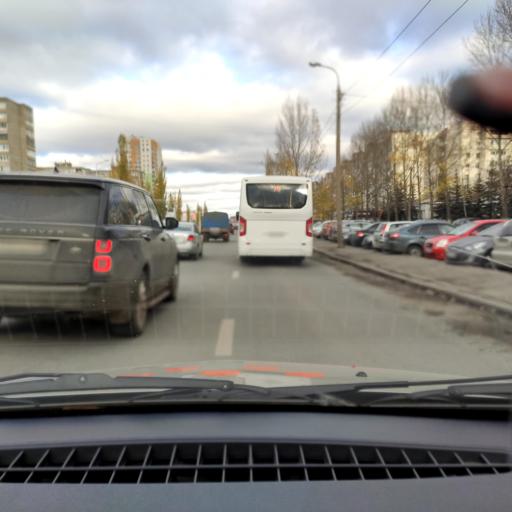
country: RU
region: Bashkortostan
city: Ufa
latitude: 54.7668
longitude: 56.0521
